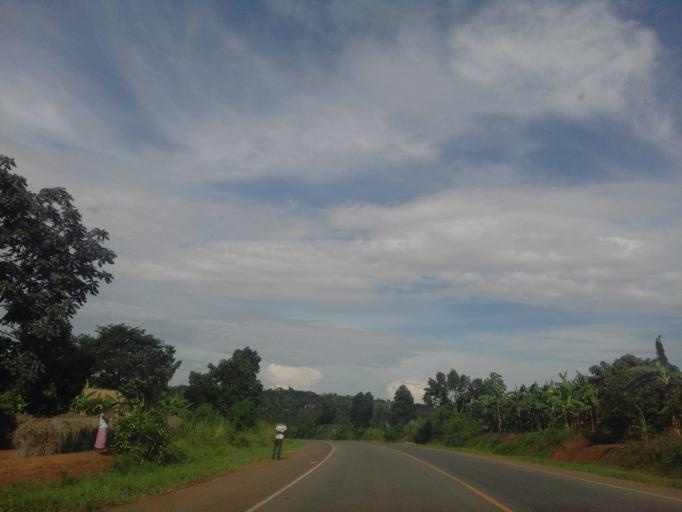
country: UG
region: Central Region
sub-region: Lwengo District
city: Lwengo
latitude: -0.3663
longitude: 31.5385
